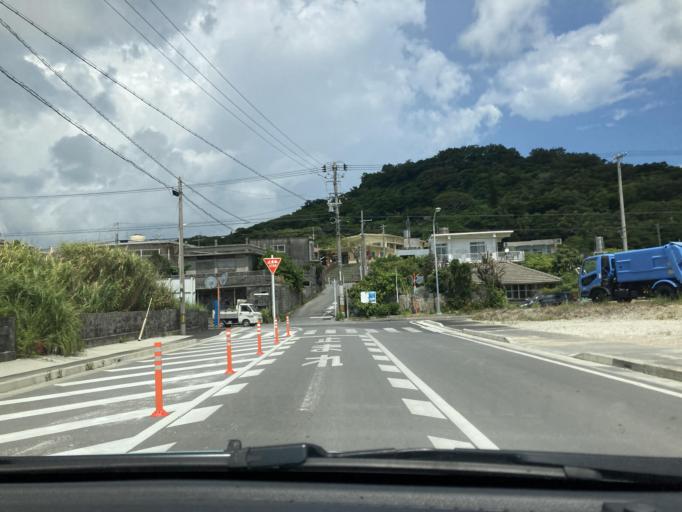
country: JP
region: Okinawa
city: Tomigusuku
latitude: 26.1631
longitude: 127.7568
